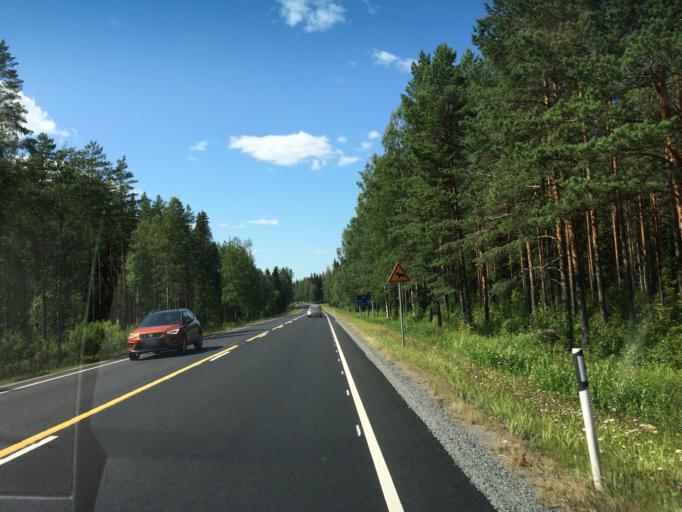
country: FI
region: Pirkanmaa
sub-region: Lounais-Pirkanmaa
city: Kiikoinen
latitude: 61.4755
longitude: 22.4653
